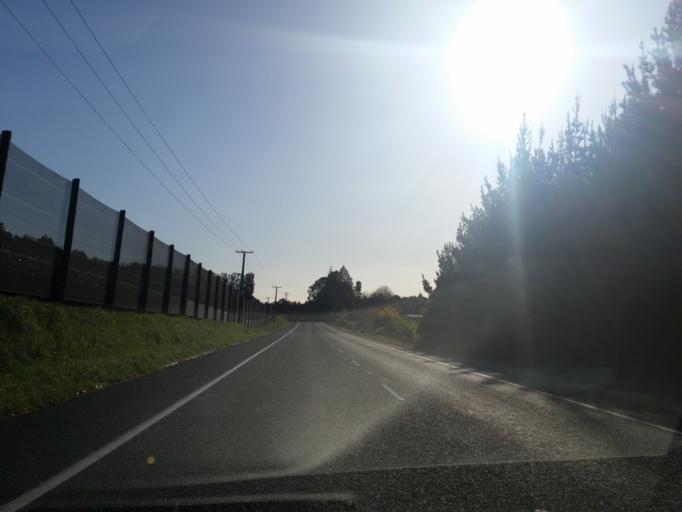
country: NZ
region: Bay of Plenty
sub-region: Western Bay of Plenty District
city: Katikati
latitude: -37.5035
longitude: 175.9242
